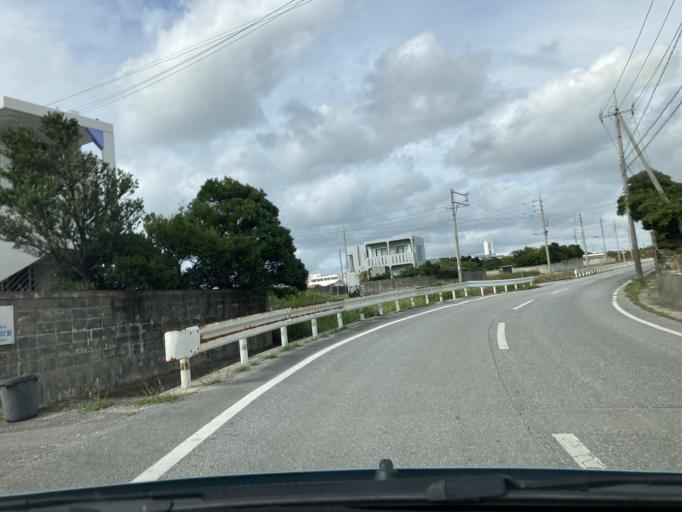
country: JP
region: Okinawa
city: Itoman
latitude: 26.1077
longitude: 127.6882
